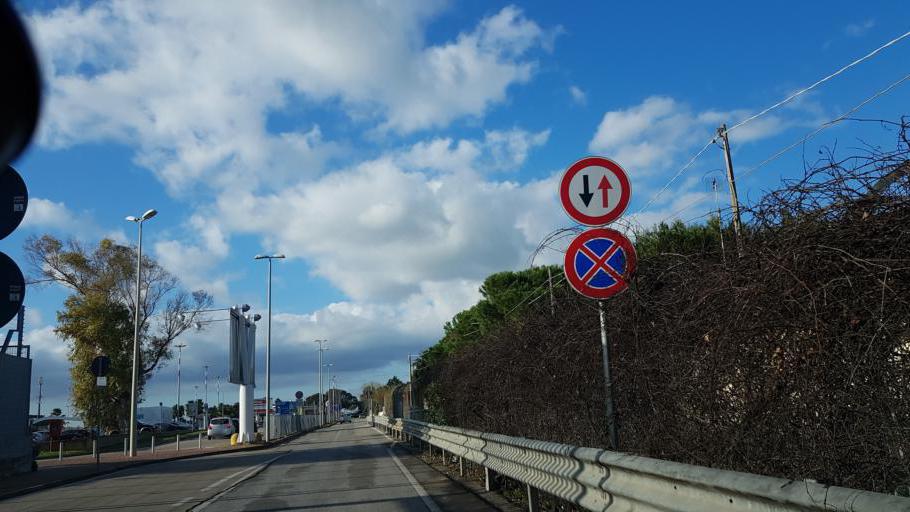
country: IT
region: Apulia
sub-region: Provincia di Brindisi
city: Materdomini
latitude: 40.6593
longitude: 17.9397
